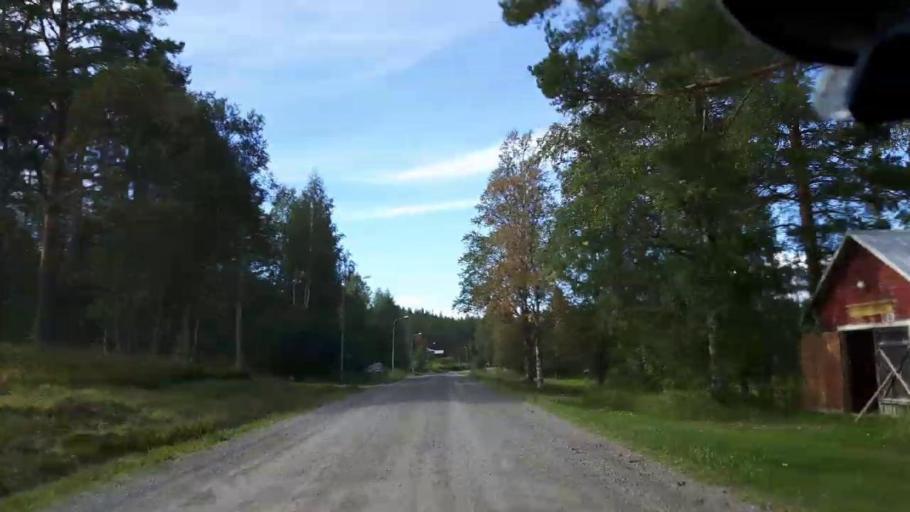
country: SE
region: Jaemtland
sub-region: Ragunda Kommun
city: Hammarstrand
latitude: 63.1449
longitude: 15.8984
